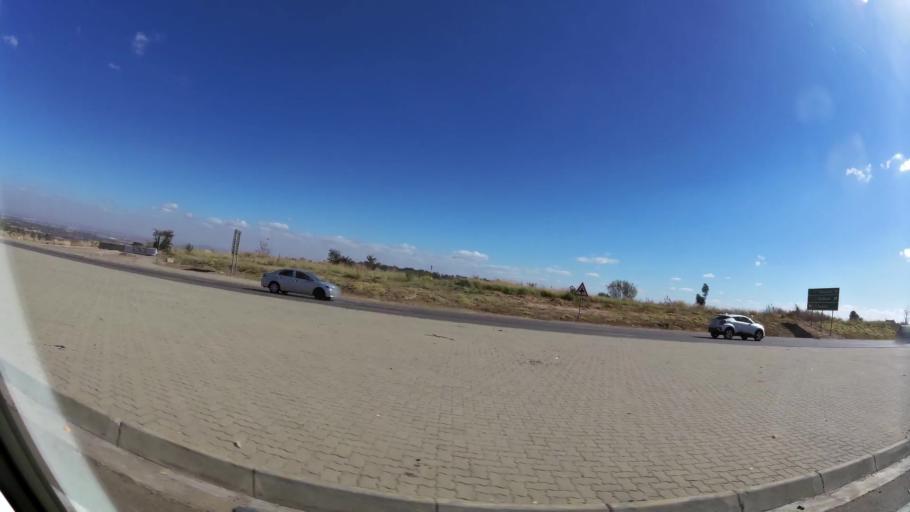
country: ZA
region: Gauteng
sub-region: City of Johannesburg Metropolitan Municipality
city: Midrand
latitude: -25.9414
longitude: 28.0946
